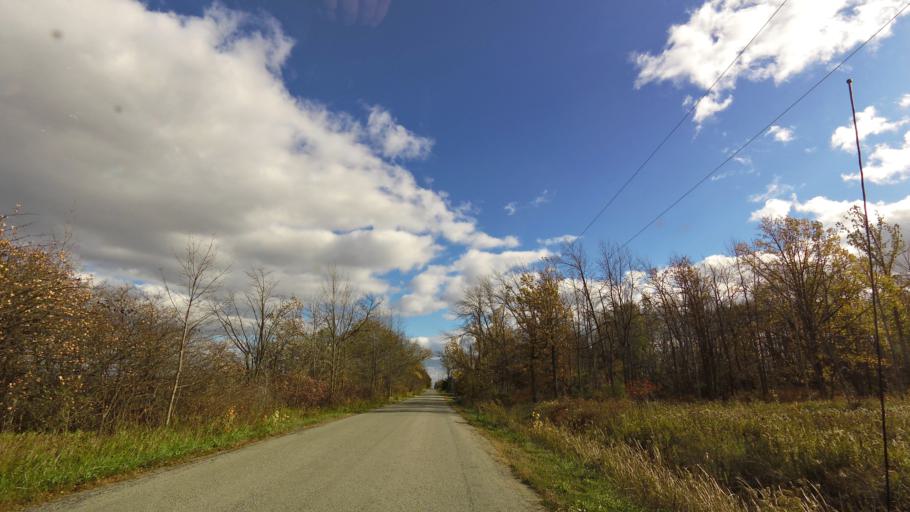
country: CA
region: Ontario
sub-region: Halton
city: Milton
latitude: 43.4541
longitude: -79.8627
